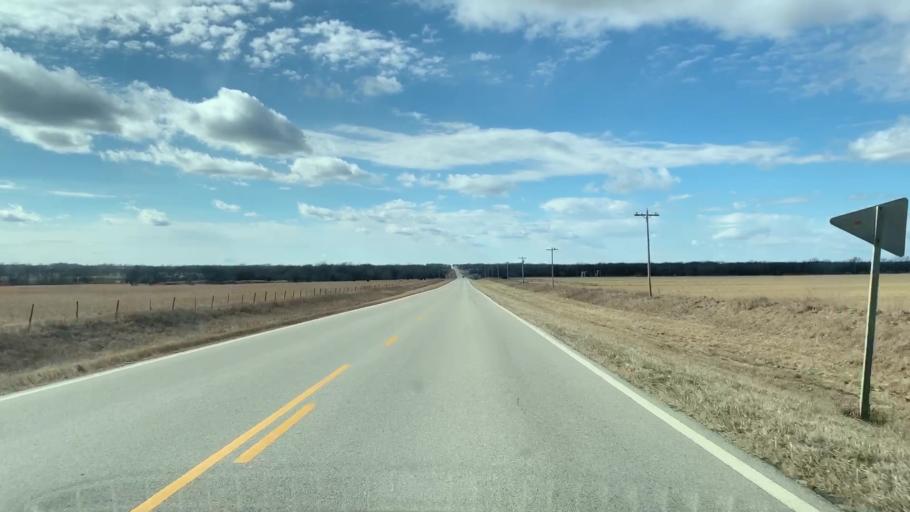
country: US
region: Kansas
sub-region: Neosho County
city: Erie
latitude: 37.5292
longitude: -95.3902
